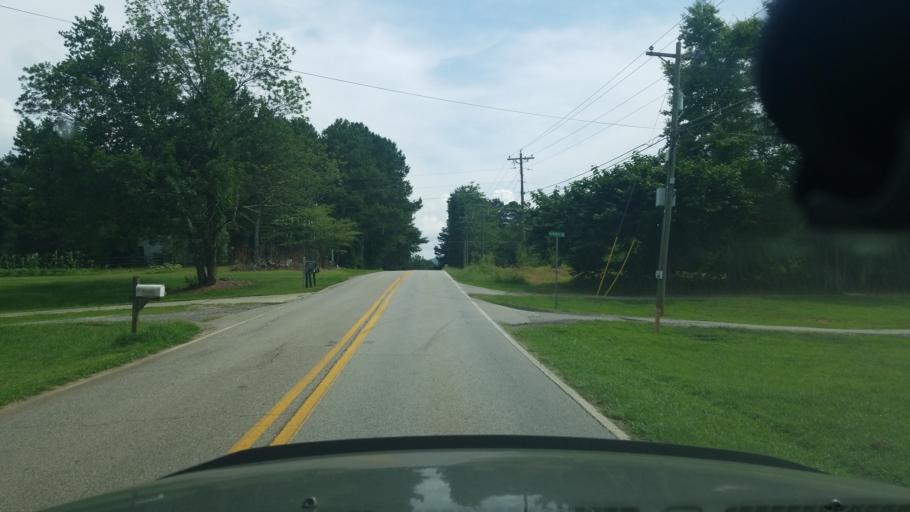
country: US
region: Georgia
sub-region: Forsyth County
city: Cumming
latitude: 34.2823
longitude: -84.1530
